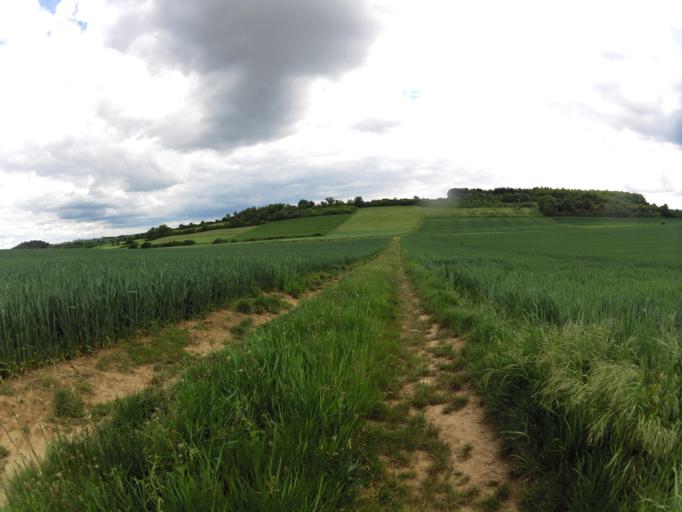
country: DE
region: Bavaria
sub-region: Regierungsbezirk Unterfranken
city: Gaukonigshofen
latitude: 49.6644
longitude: 10.0031
